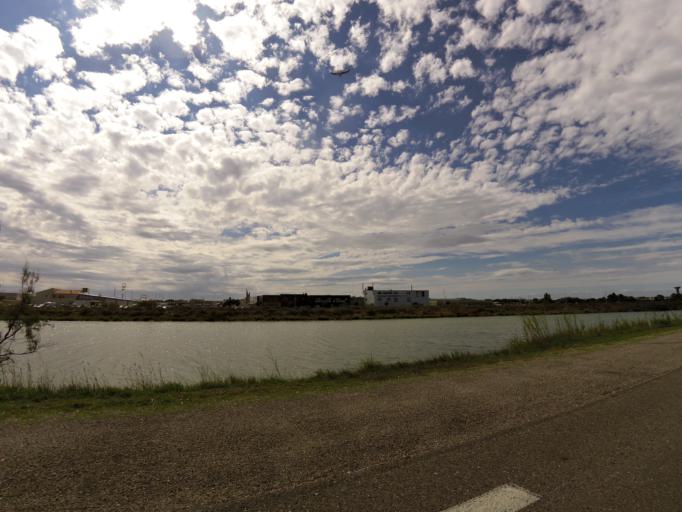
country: FR
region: Languedoc-Roussillon
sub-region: Departement du Gard
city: Le Grau-du-Roi
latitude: 43.5421
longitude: 4.1412
